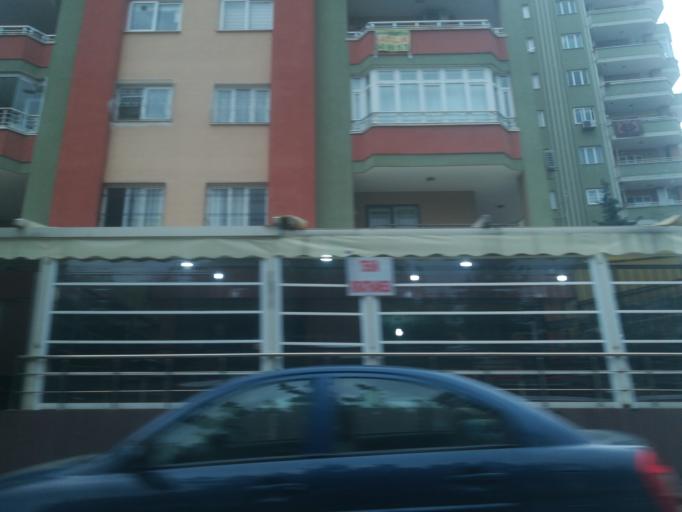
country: TR
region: Adana
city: Adana
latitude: 37.0369
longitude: 35.2939
